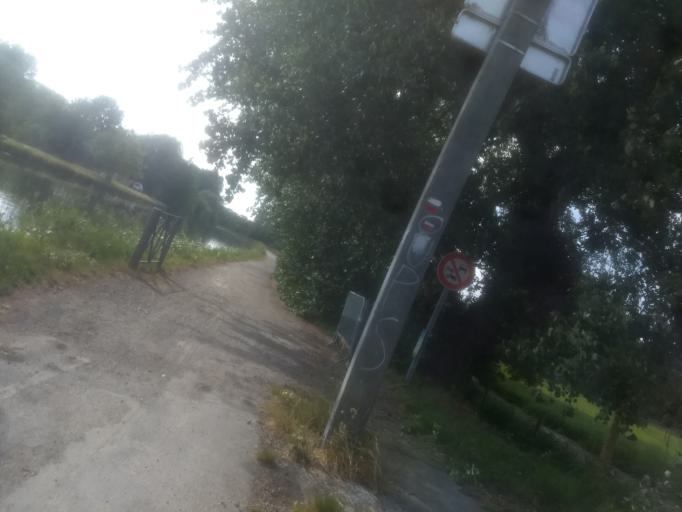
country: FR
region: Nord-Pas-de-Calais
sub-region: Departement du Pas-de-Calais
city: Feuchy
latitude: 50.2990
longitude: 2.8363
